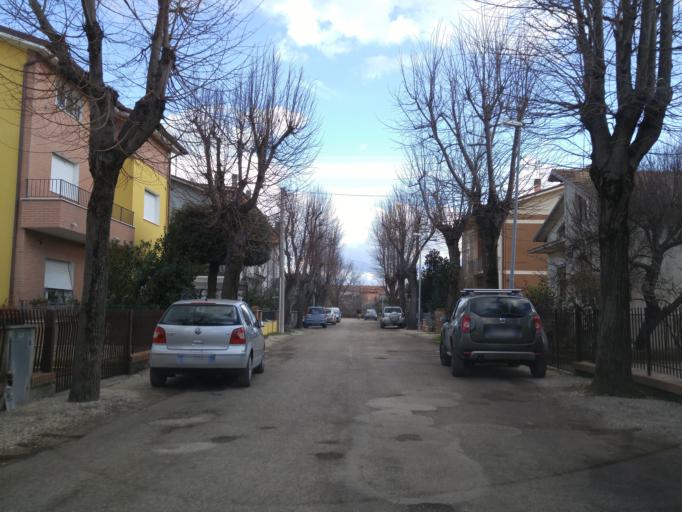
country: IT
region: The Marches
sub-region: Provincia di Pesaro e Urbino
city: Rosciano
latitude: 43.8258
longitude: 13.0016
